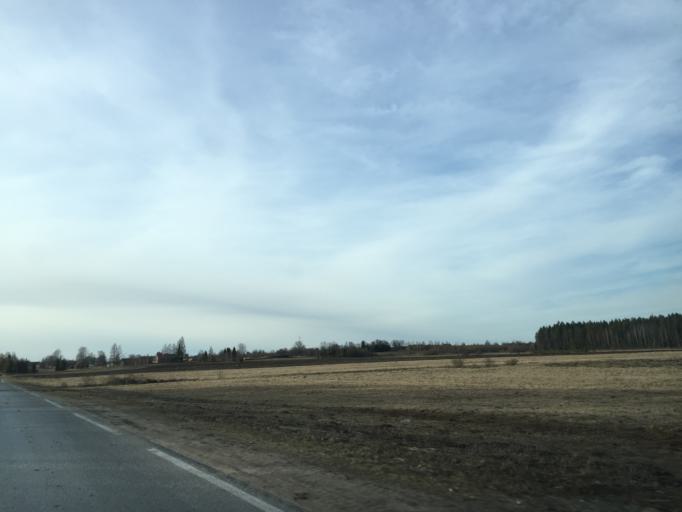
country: LV
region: Krimulda
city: Ragana
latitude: 57.1736
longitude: 24.7265
